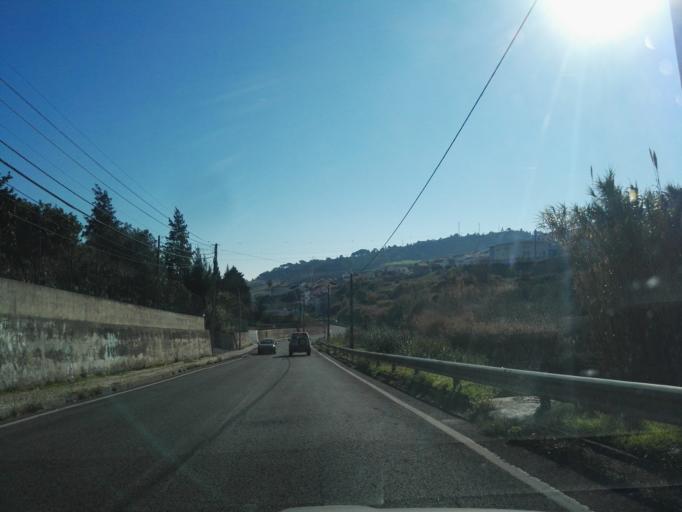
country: PT
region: Lisbon
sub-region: Vila Franca de Xira
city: Sao Joao dos Montes
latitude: 38.9353
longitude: -9.0232
